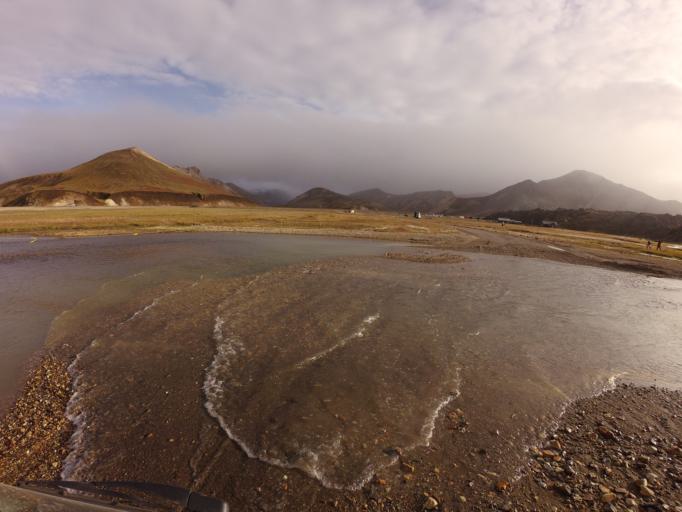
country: IS
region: South
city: Vestmannaeyjar
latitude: 63.9938
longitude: -19.0600
